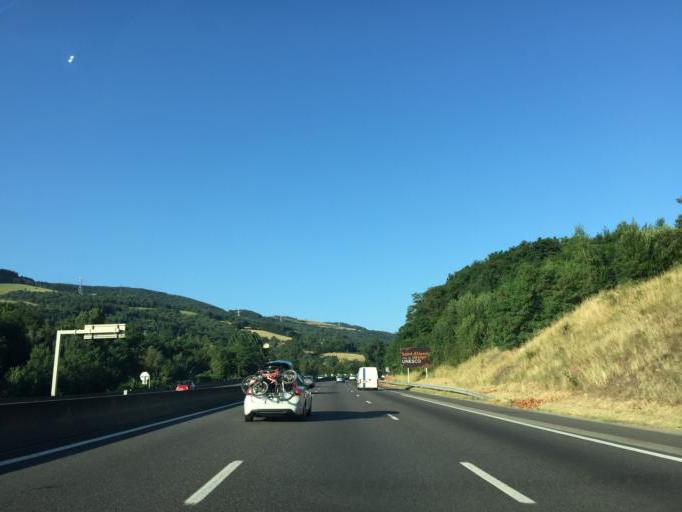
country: FR
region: Rhone-Alpes
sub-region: Departement de la Loire
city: Saint-Jean-Bonnefonds
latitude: 45.4443
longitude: 4.4651
